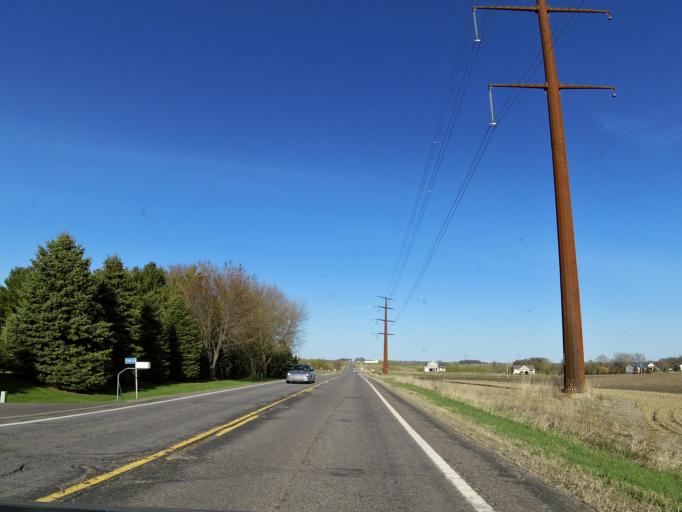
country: US
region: Minnesota
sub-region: Scott County
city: Elko New Market
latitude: 44.5728
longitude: -93.4038
